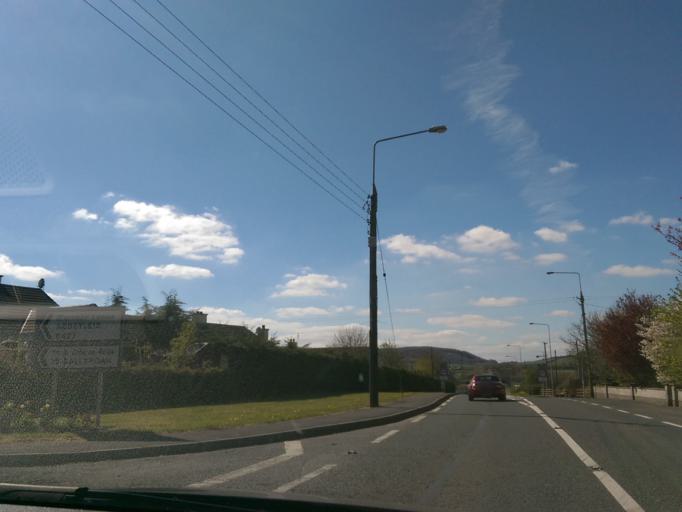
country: IE
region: Leinster
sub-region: Laois
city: Stradbally
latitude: 53.0192
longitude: -7.1555
